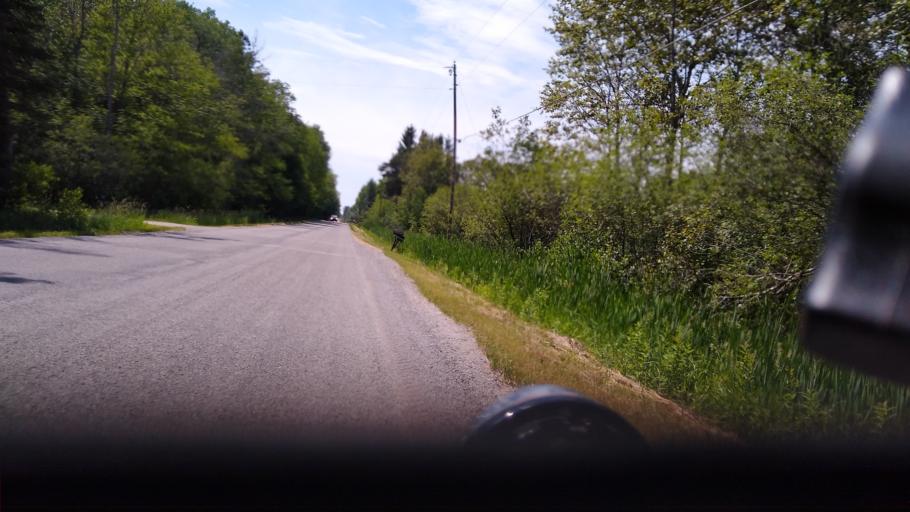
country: US
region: Michigan
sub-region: Delta County
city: Escanaba
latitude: 45.7102
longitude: -87.1363
